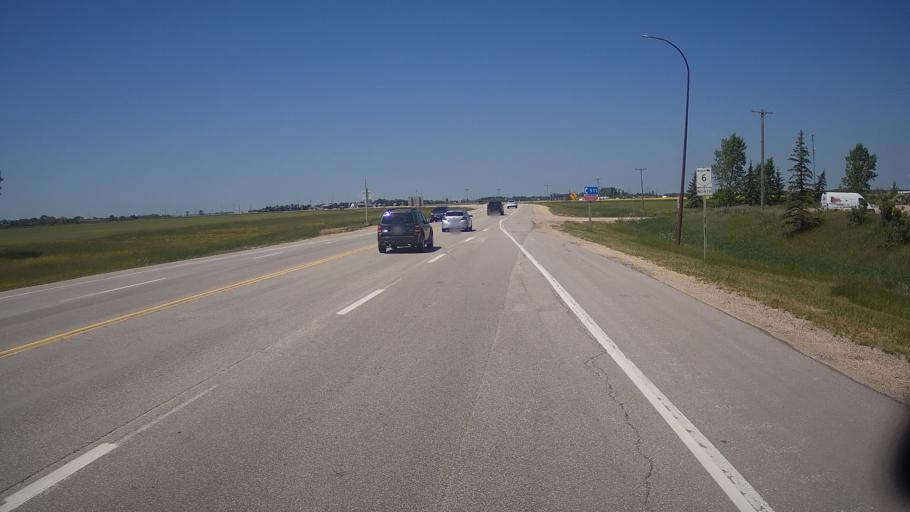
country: CA
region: Manitoba
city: Stonewall
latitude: 49.9879
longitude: -97.3110
